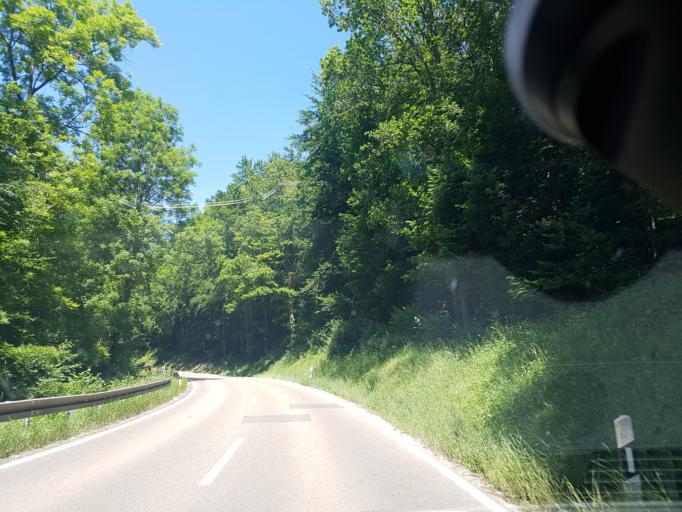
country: DE
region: Baden-Wuerttemberg
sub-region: Tuebingen Region
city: Dornstadt
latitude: 48.4198
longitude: 9.8860
